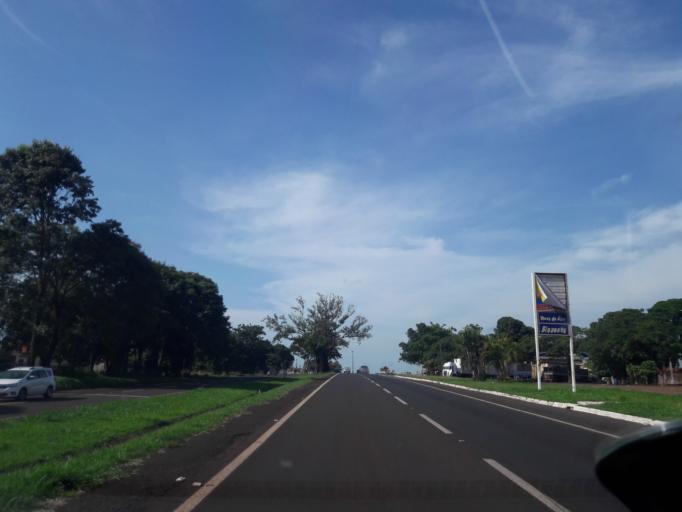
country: BR
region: Parana
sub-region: Paicandu
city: Paicandu
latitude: -23.6105
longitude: -52.0873
